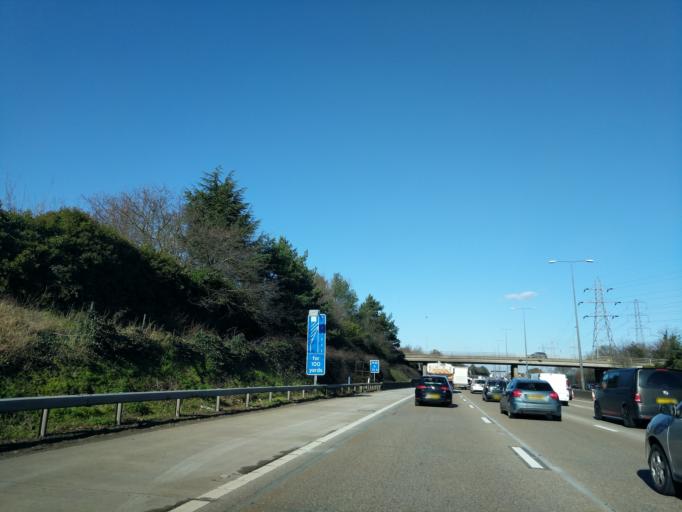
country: GB
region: England
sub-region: Surrey
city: Byfleet
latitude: 51.3387
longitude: -0.4852
